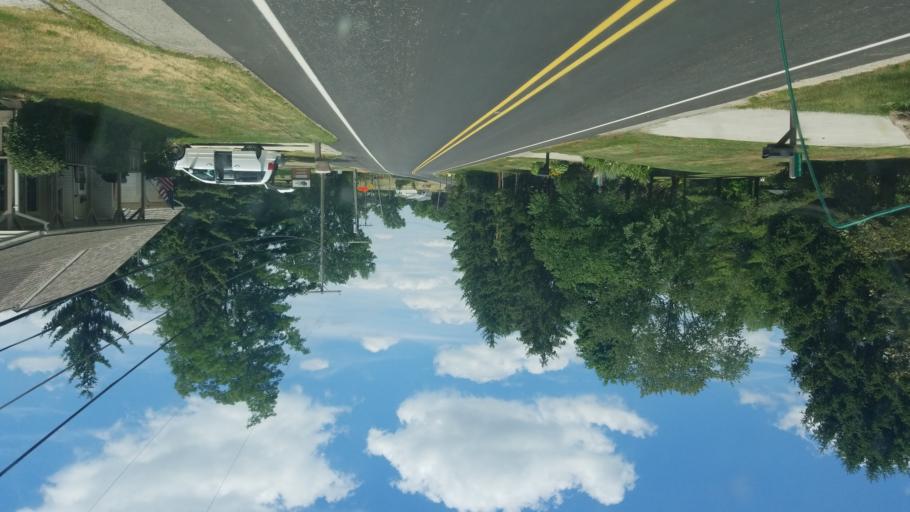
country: US
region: Indiana
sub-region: Allen County
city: Harlan
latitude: 41.2001
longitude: -84.9108
